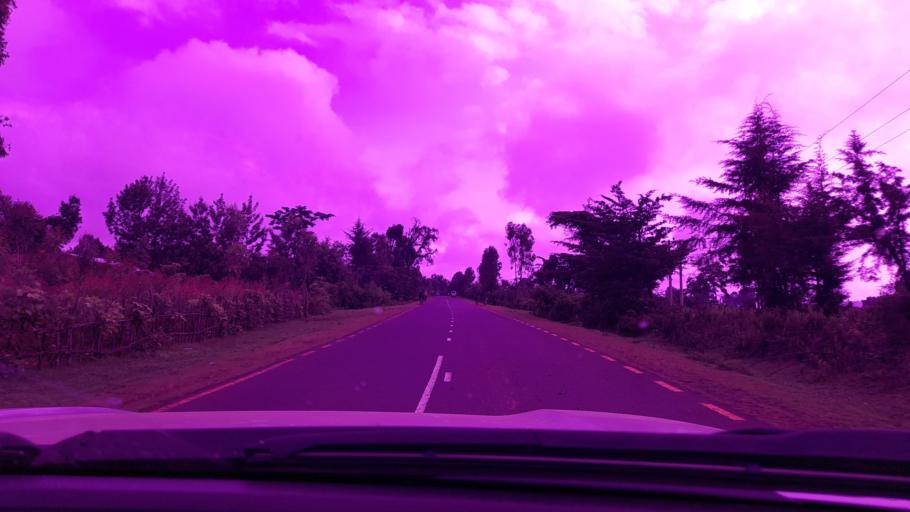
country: ET
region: Oromiya
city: Bedele
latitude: 8.2993
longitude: 36.4494
